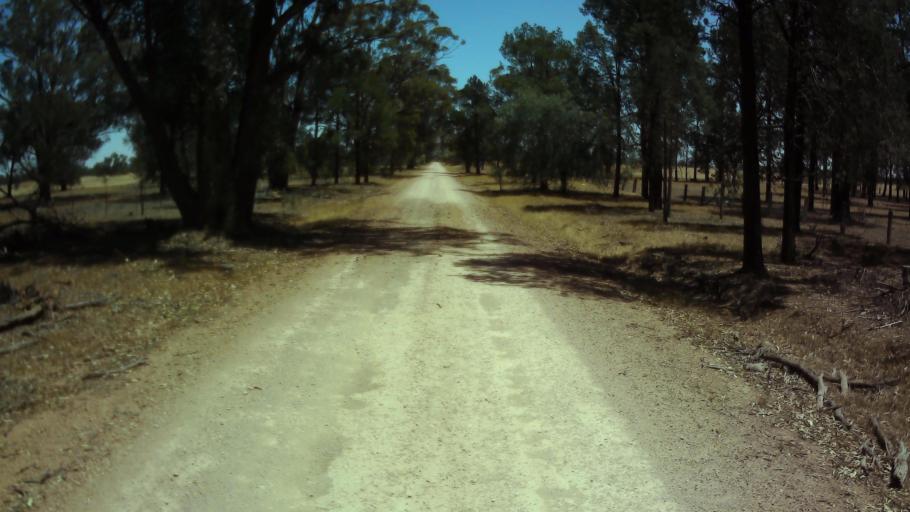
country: AU
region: New South Wales
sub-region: Weddin
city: Grenfell
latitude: -33.9902
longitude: 147.9402
